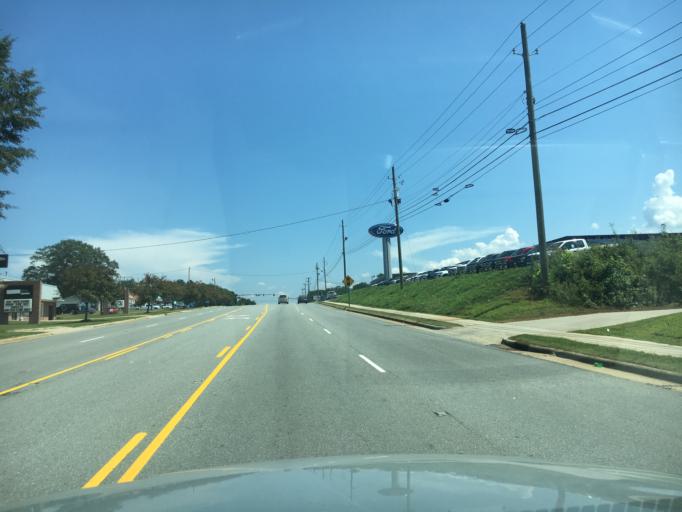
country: US
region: North Carolina
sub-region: Rutherford County
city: Forest City
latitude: 35.3335
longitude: -81.8846
